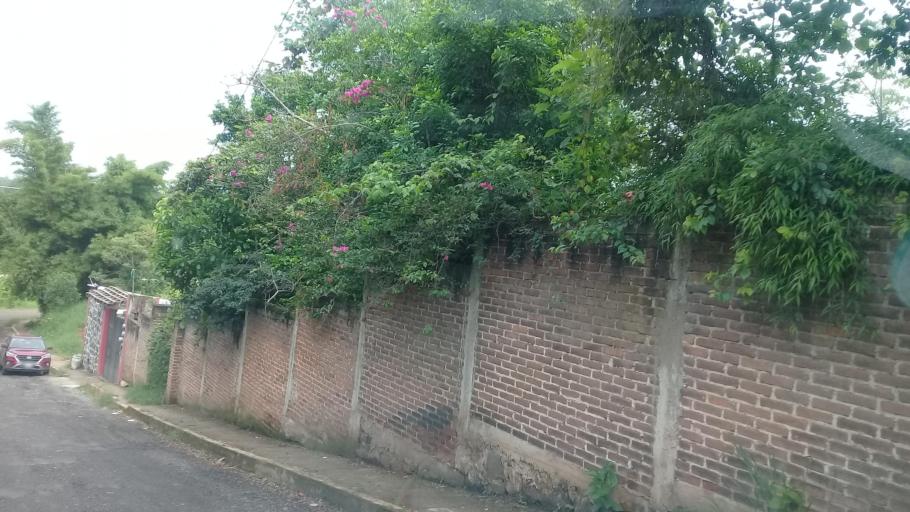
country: MX
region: Veracruz
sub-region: Emiliano Zapata
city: Jacarandas
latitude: 19.4811
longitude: -96.8559
